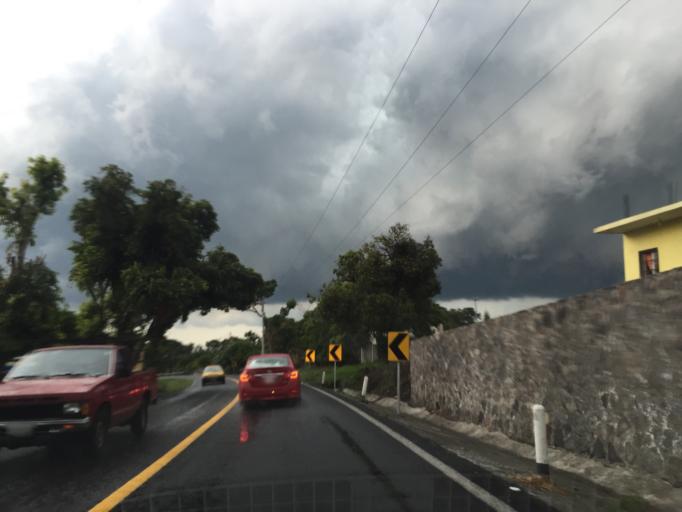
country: MX
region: Colima
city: Queseria
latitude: 19.3674
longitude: -103.5796
